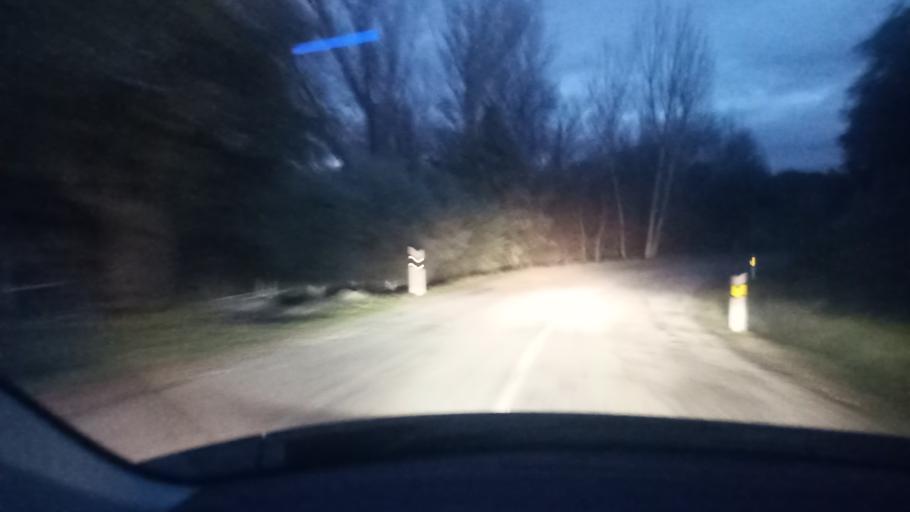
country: ES
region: Madrid
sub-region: Provincia de Madrid
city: Colmenar del Arroyo
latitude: 40.4266
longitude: -4.2049
